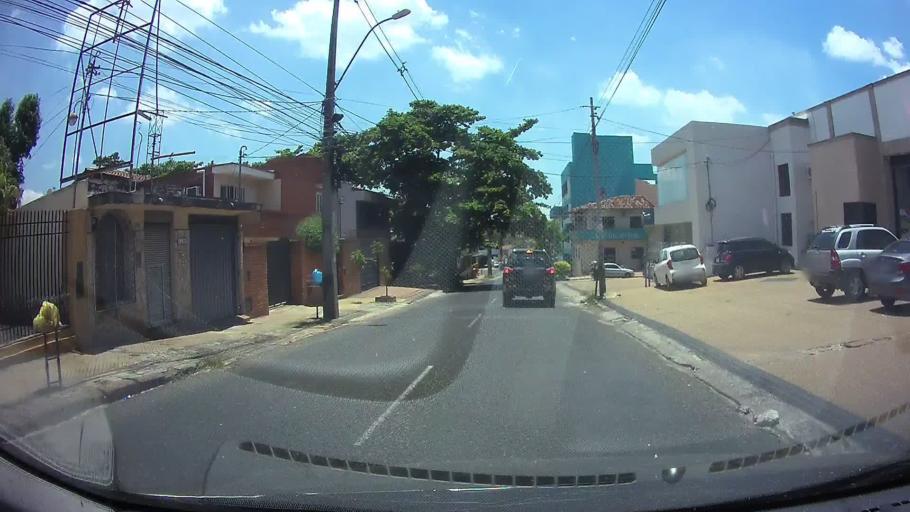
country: PY
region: Asuncion
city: Asuncion
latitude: -25.2951
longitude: -57.5912
